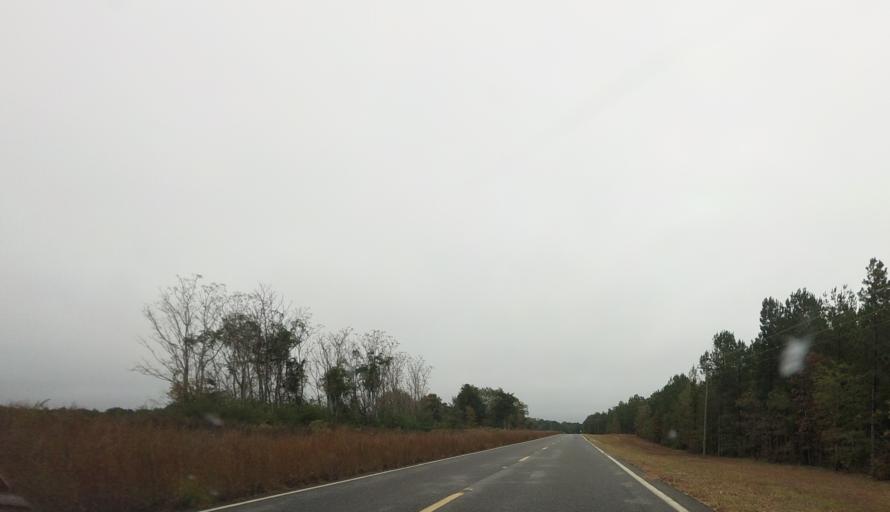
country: US
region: Georgia
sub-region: Taylor County
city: Butler
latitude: 32.4349
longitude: -84.3256
